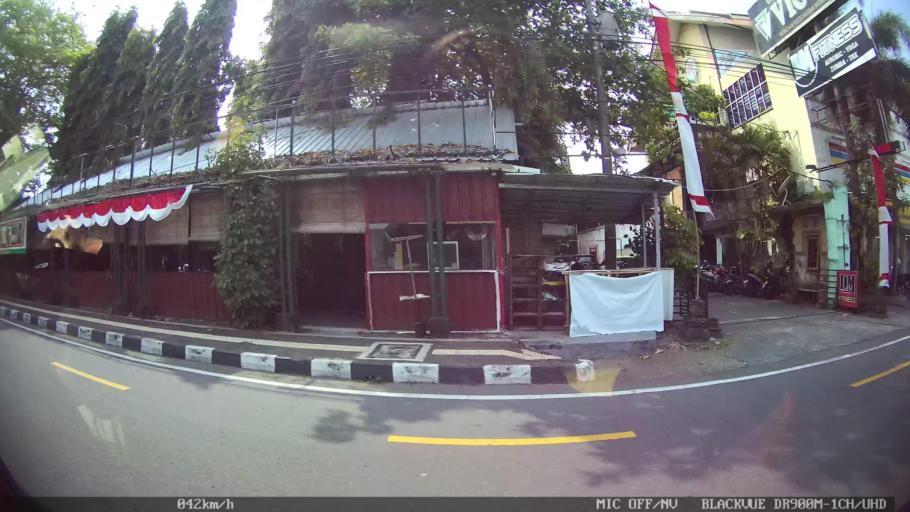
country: ID
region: Daerah Istimewa Yogyakarta
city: Yogyakarta
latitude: -7.8039
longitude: 110.3949
